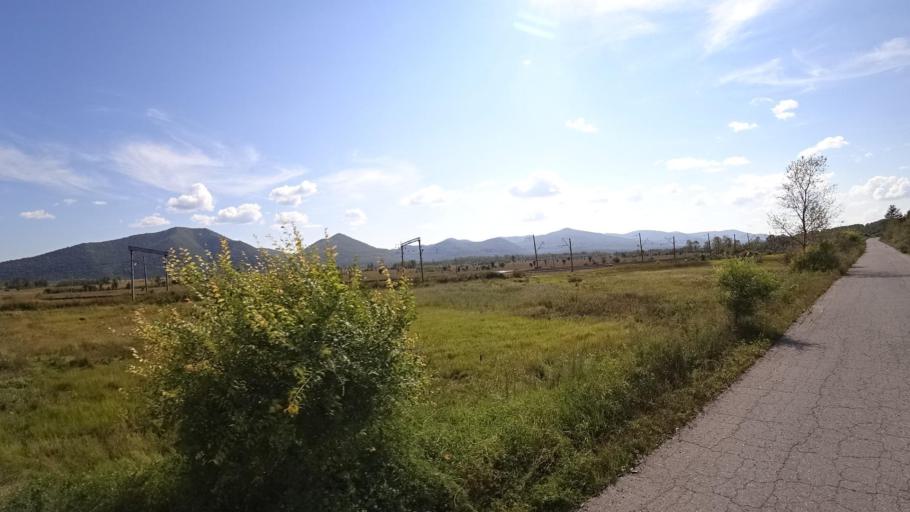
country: RU
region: Jewish Autonomous Oblast
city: Londoko
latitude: 49.0014
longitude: 131.8632
